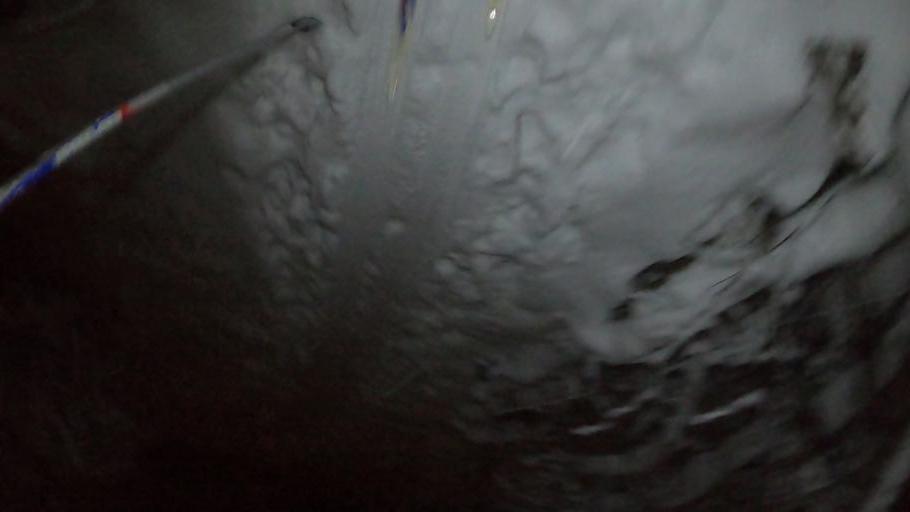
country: RU
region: Moskovskaya
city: Opalikha
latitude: 55.8587
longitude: 37.2335
